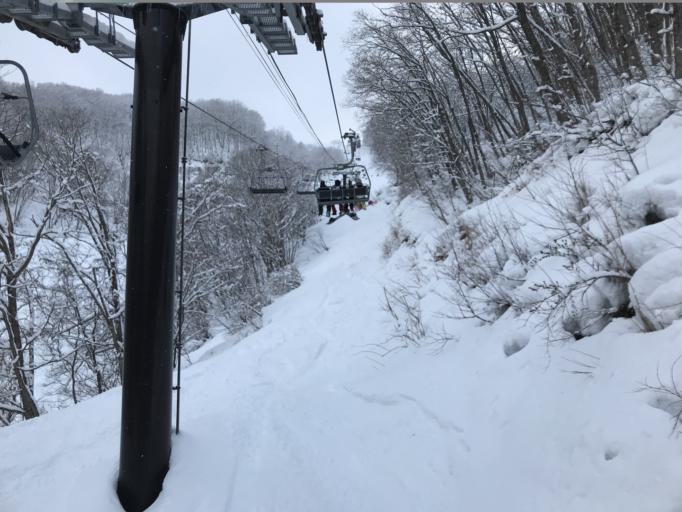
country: JP
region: Nagano
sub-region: Kitaazumi Gun
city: Hakuba
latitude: 36.7103
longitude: 137.8248
